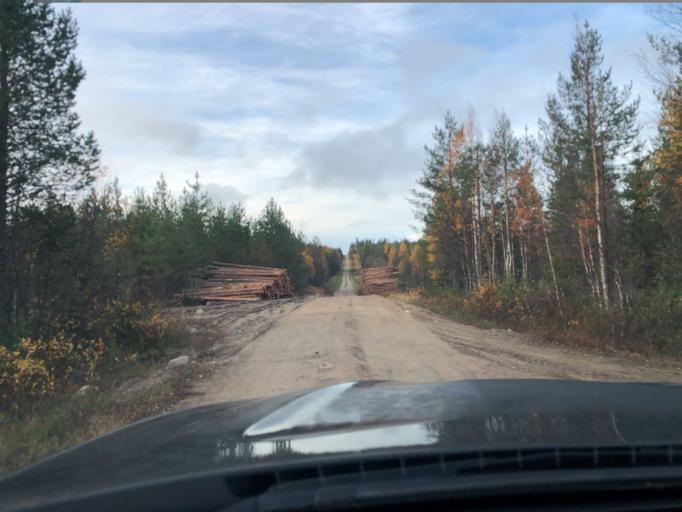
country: FI
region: Lapland
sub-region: Itae-Lappi
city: Posio
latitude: 66.1007
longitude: 28.5425
